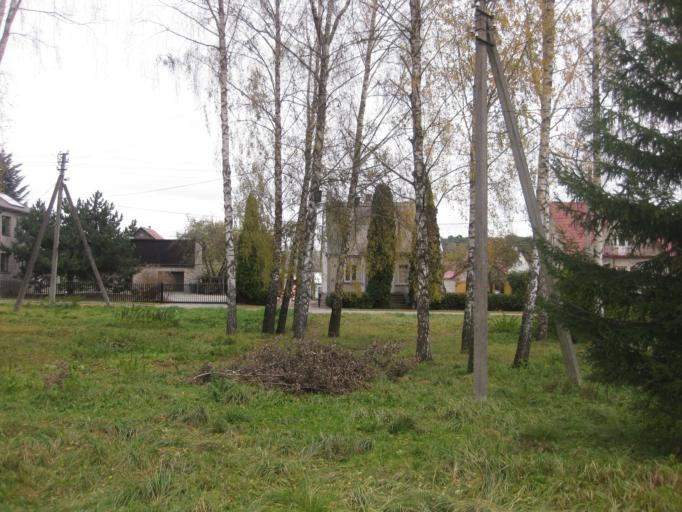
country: LT
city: Prienai
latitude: 54.6406
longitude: 23.9430
